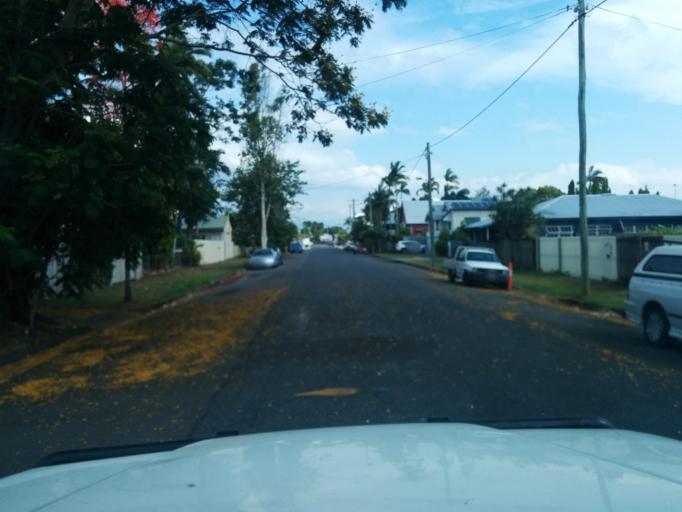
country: AU
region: Queensland
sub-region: Cairns
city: Cairns
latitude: -16.9221
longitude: 145.7627
